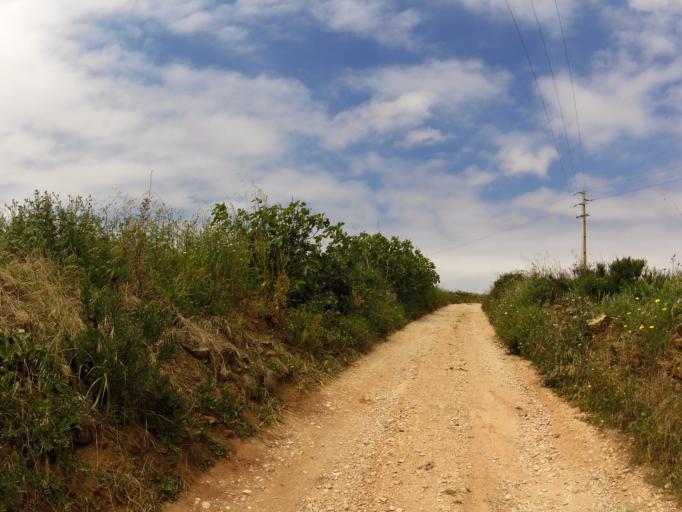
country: PT
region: Faro
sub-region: Vila do Bispo
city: Vila do Bispo
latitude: 37.0845
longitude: -8.8915
